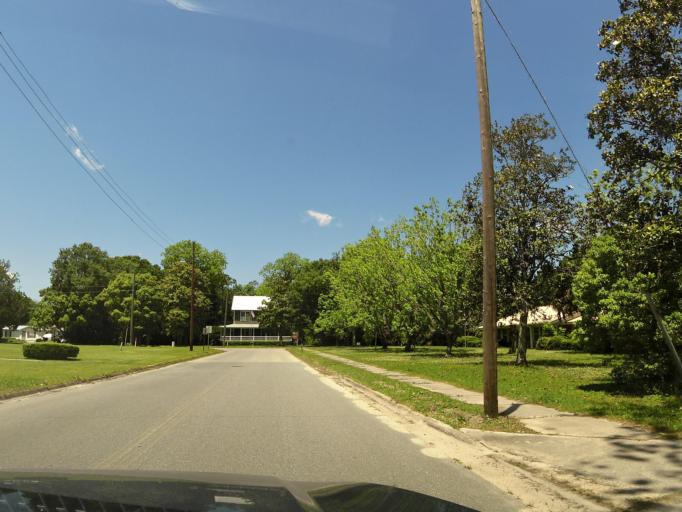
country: US
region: Florida
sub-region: Bradford County
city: Starke
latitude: 30.0454
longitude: -82.0754
